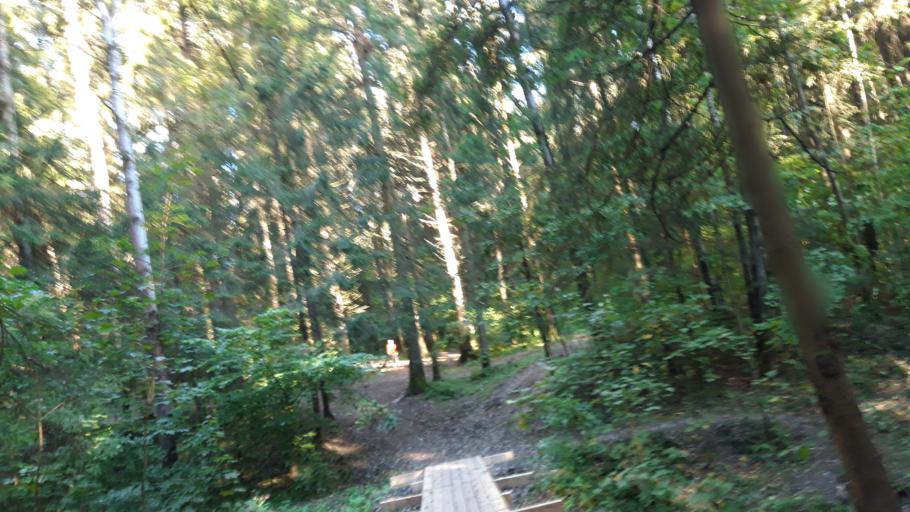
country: RU
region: Moscow
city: Zelenograd
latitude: 55.9854
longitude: 37.1965
